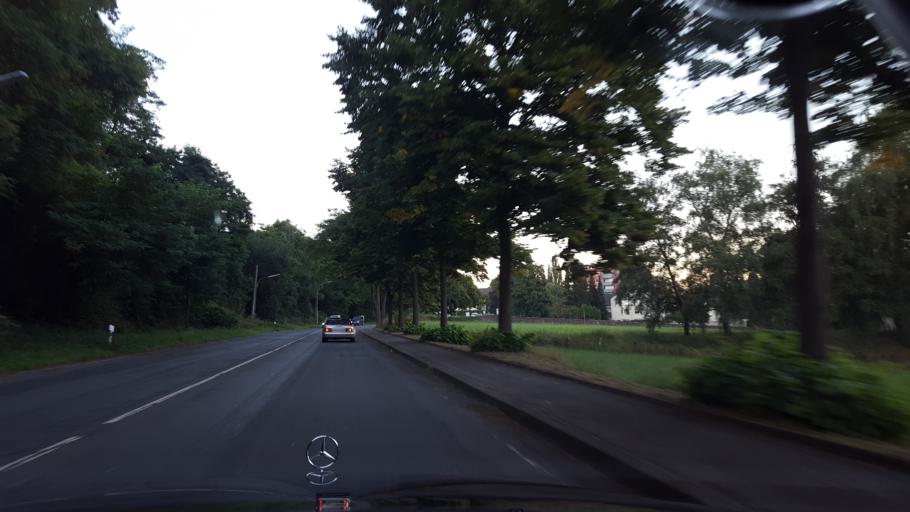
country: DE
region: North Rhine-Westphalia
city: Witten
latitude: 51.4534
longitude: 7.3698
